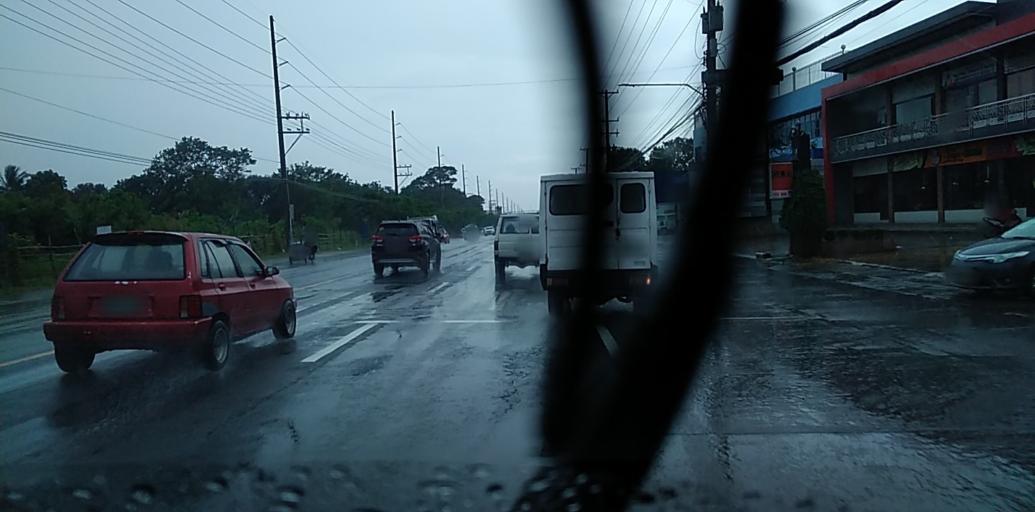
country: PH
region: Central Luzon
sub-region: Province of Pampanga
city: Magliman
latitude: 15.0588
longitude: 120.6571
